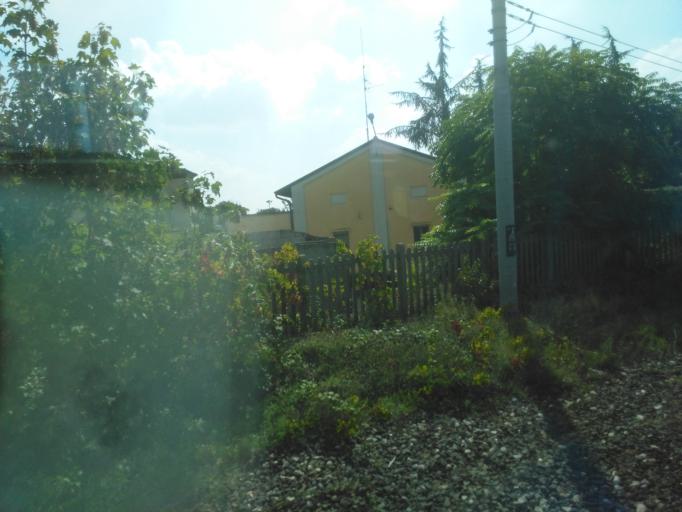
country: IT
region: Lombardy
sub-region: Provincia di Brescia
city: Chiari
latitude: 45.5391
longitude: 9.9218
